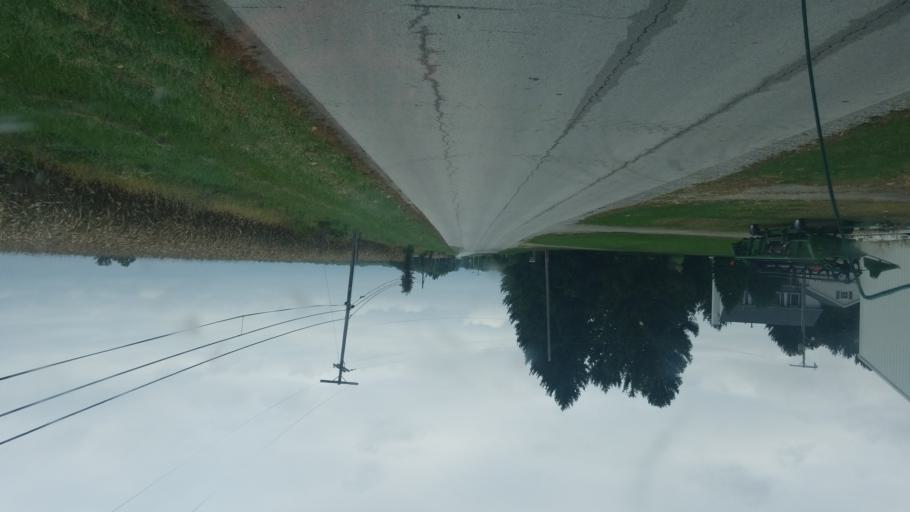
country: US
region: Ohio
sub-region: Wood County
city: Bowling Green
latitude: 41.2852
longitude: -83.6695
